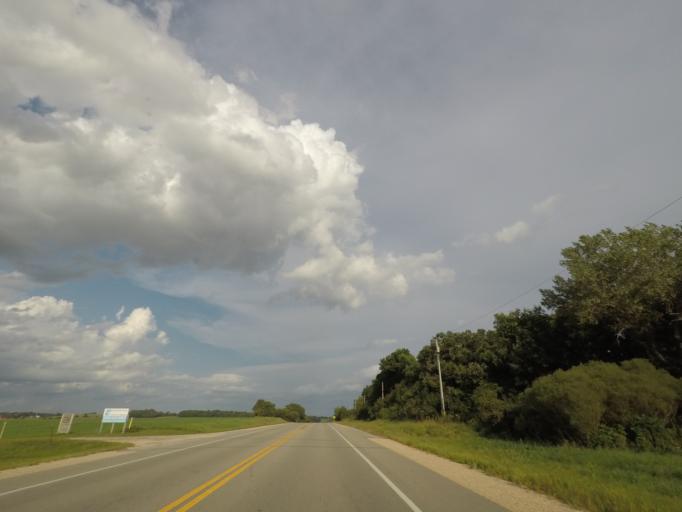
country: US
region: Wisconsin
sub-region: Dane County
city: Waunakee
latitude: 43.1918
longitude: -89.5251
